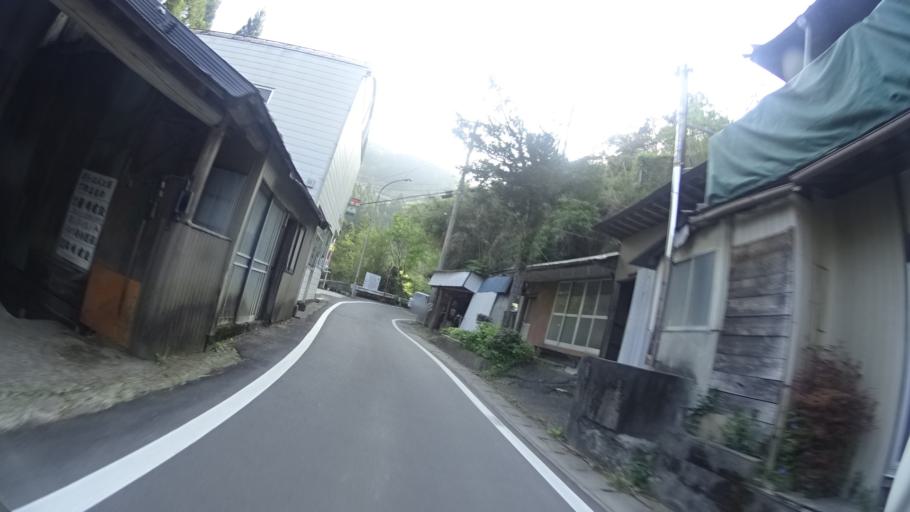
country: JP
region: Tokushima
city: Ikedacho
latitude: 33.8800
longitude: 133.9346
